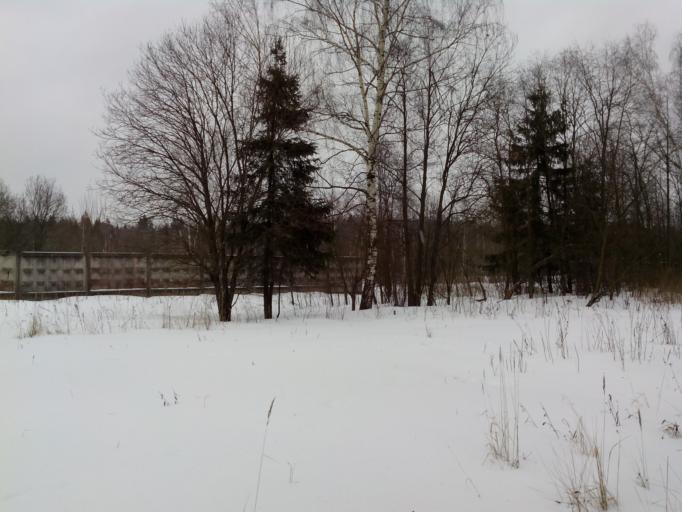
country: RU
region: Moskovskaya
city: Bol'shiye Vyazemy
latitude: 55.6701
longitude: 36.9691
